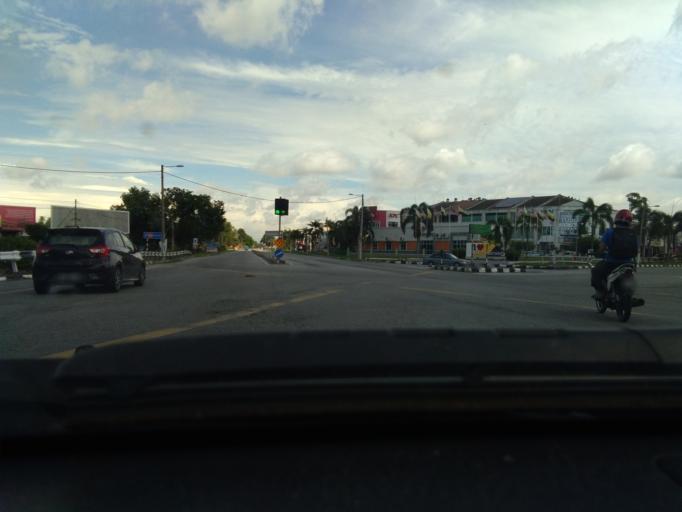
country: MY
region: Perak
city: Parit Buntar
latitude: 5.1109
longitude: 100.4821
